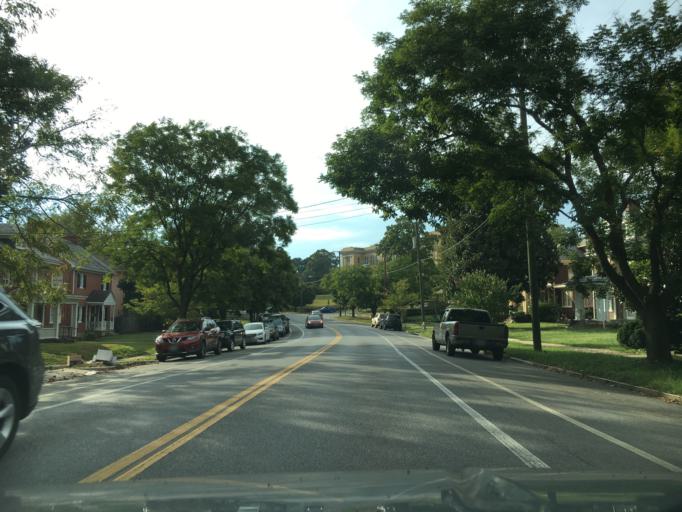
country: US
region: Virginia
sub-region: City of Lynchburg
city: Lynchburg
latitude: 37.4364
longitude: -79.1639
